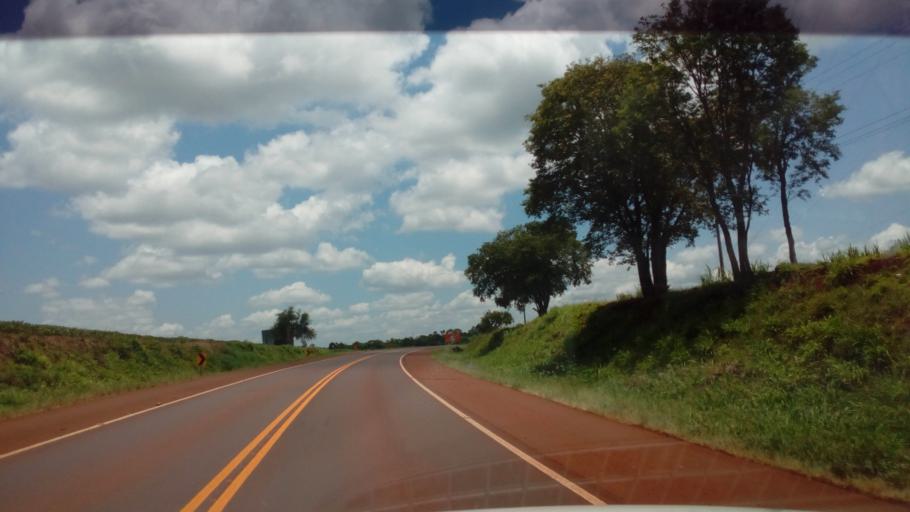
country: PY
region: Itapua
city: Arquitecto Tomas Romero Pereira
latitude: -26.4452
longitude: -55.2494
